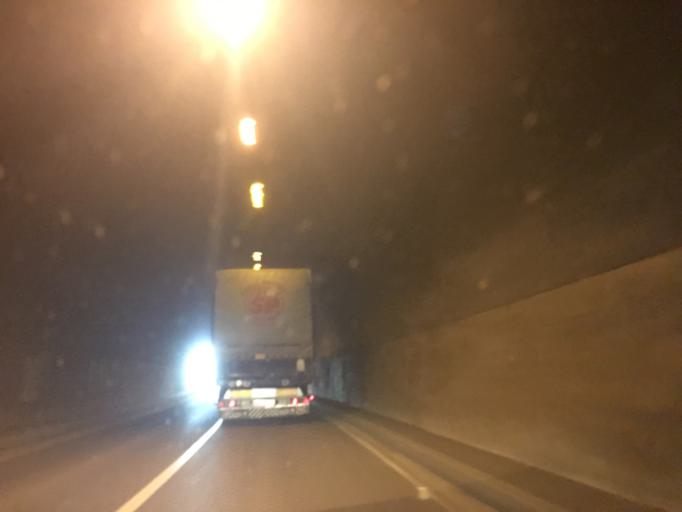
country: BA
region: Republika Srpska
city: Pale
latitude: 43.8401
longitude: 18.4871
